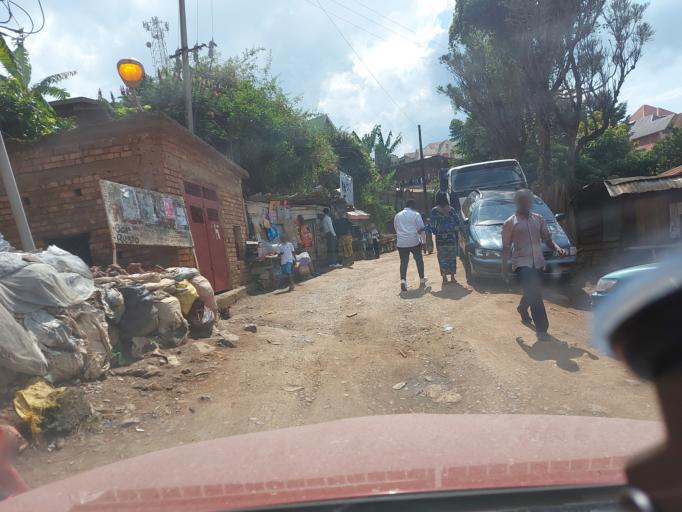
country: RW
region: Western Province
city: Cyangugu
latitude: -2.5011
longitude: 28.8782
